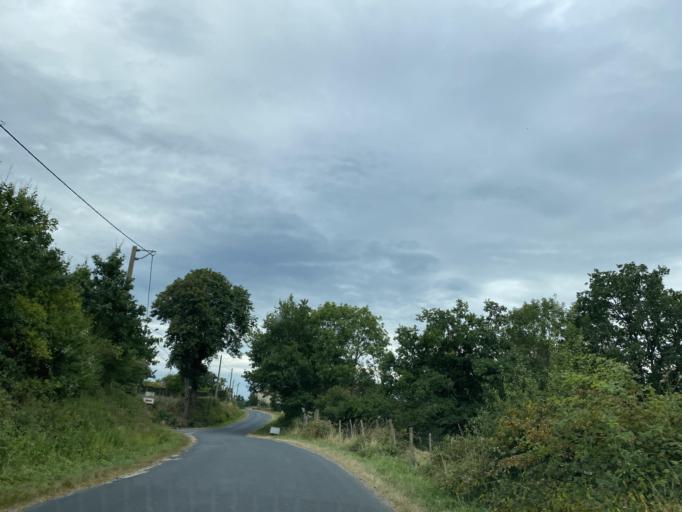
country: FR
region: Auvergne
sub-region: Departement du Puy-de-Dome
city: Marsac-en-Livradois
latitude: 45.4961
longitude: 3.7405
